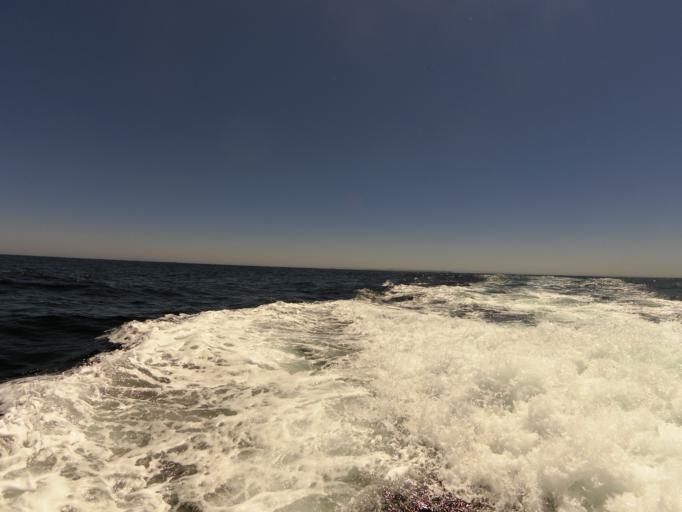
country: PT
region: Leiria
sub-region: Peniche
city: Peniche
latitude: 39.3925
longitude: -9.4757
